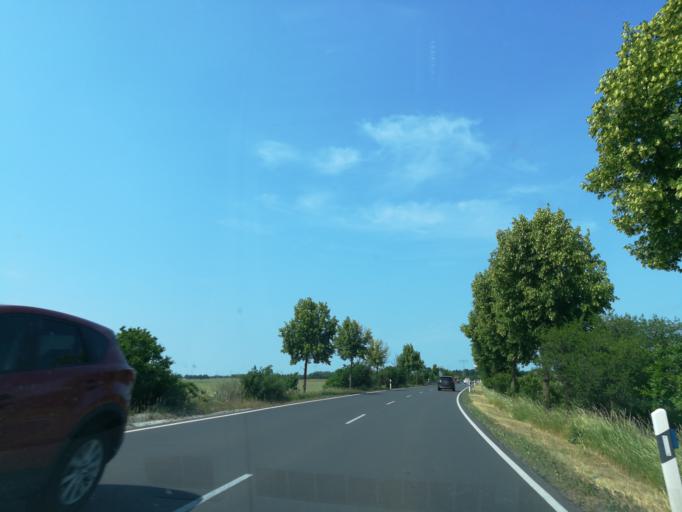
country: DE
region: Saxony-Anhalt
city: Egeln
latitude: 51.9258
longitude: 11.4209
